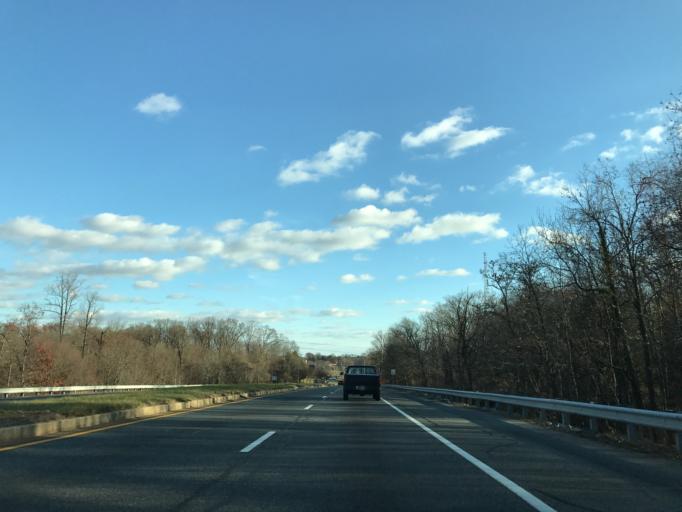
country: US
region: Maryland
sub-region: Harford County
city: Joppatowne
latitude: 39.4376
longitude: -76.3441
